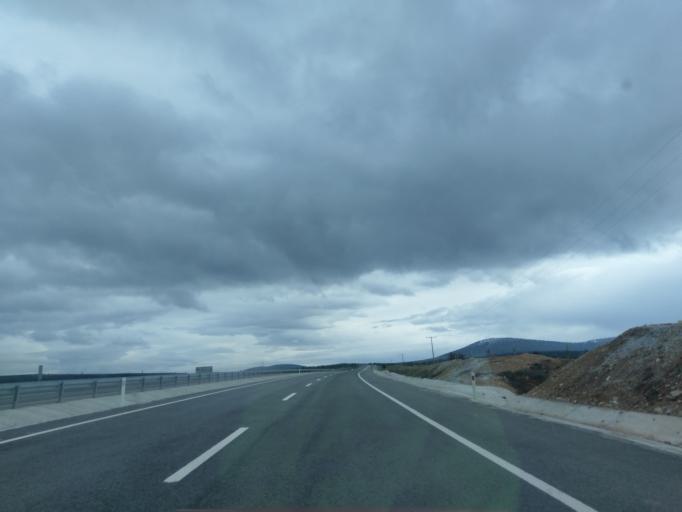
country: TR
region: Kuetahya
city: Cavdarhisar
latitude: 39.2261
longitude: 29.7179
